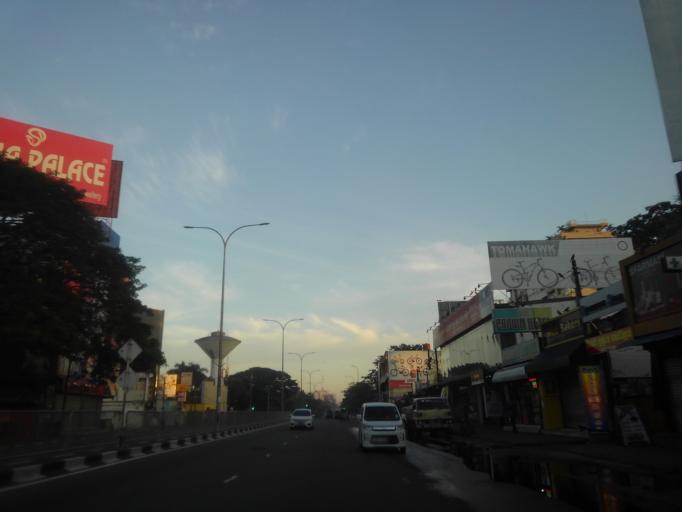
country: LK
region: Western
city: Kolonnawa
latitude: 6.9157
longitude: 79.8777
